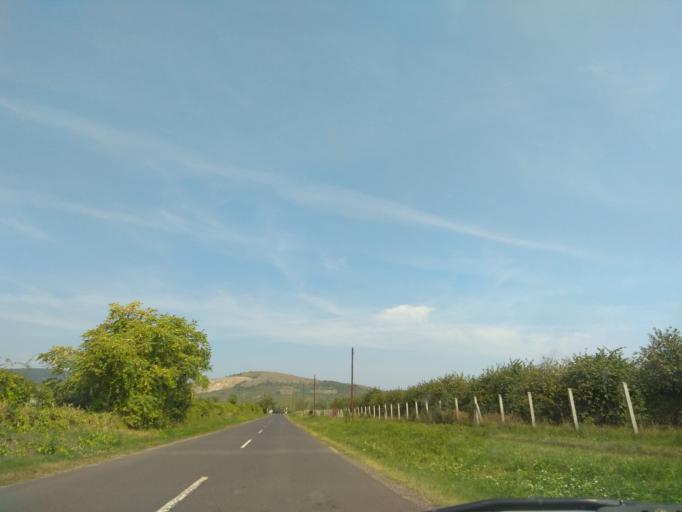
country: HU
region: Borsod-Abauj-Zemplen
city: Tallya
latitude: 48.2249
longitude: 21.2315
